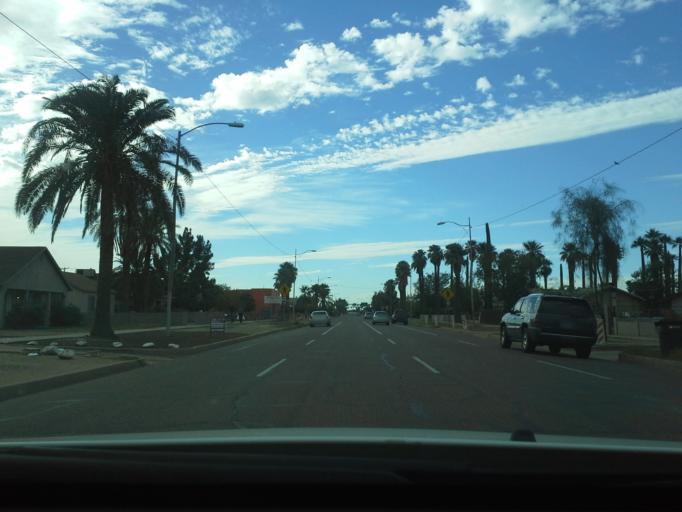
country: US
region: Arizona
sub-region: Maricopa County
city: Phoenix
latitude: 33.4492
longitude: -112.1033
